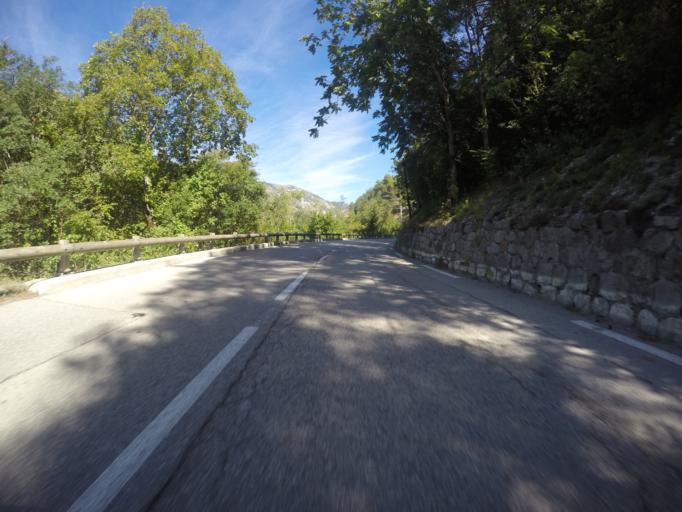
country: FR
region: Provence-Alpes-Cote d'Azur
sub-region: Departement des Alpes-Maritimes
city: Gilette
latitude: 43.9583
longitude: 7.1565
